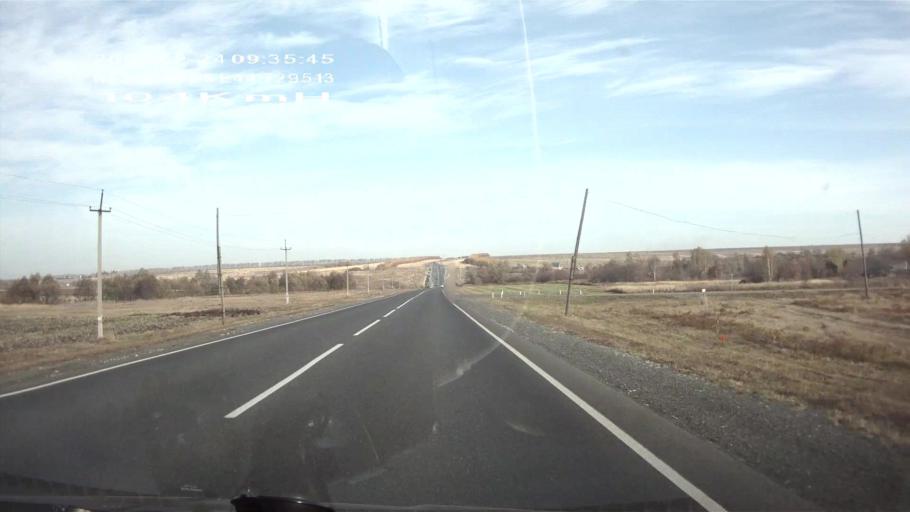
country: RU
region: Penza
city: Mokshan
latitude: 53.6087
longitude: 44.7296
